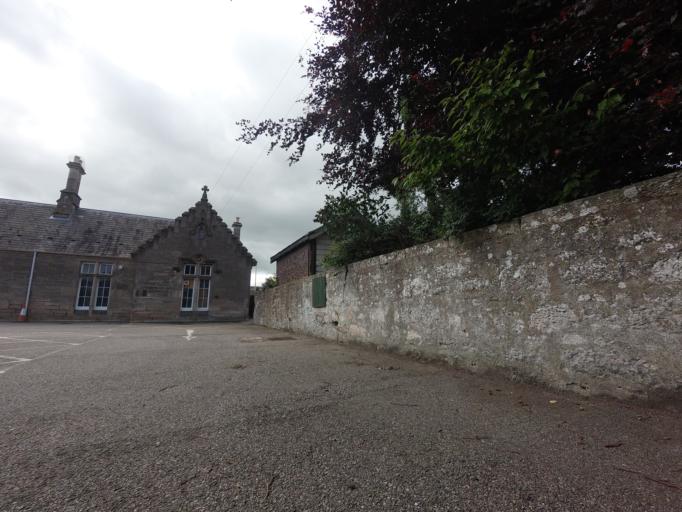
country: GB
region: Scotland
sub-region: Highland
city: Nairn
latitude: 57.5800
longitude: -3.8723
